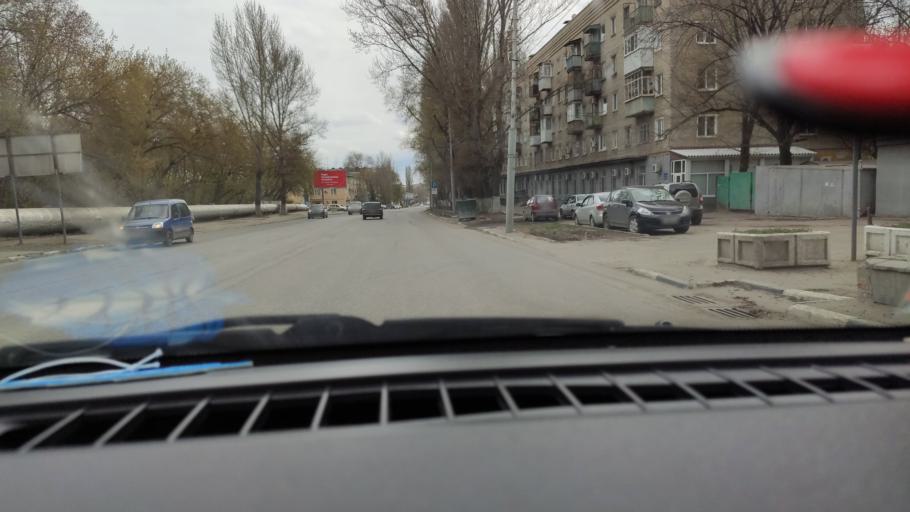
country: RU
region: Saratov
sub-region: Saratovskiy Rayon
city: Saratov
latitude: 51.5531
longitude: 46.0089
